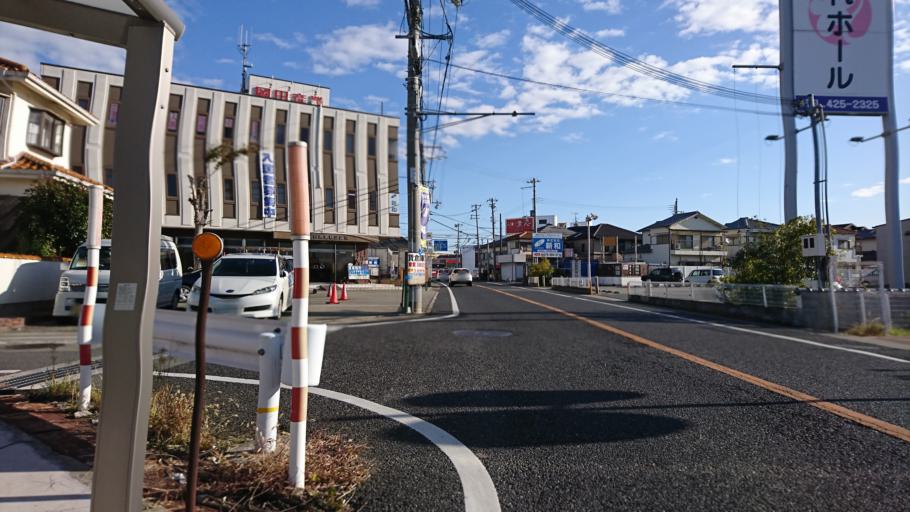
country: JP
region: Hyogo
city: Kakogawacho-honmachi
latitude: 34.7531
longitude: 134.8511
